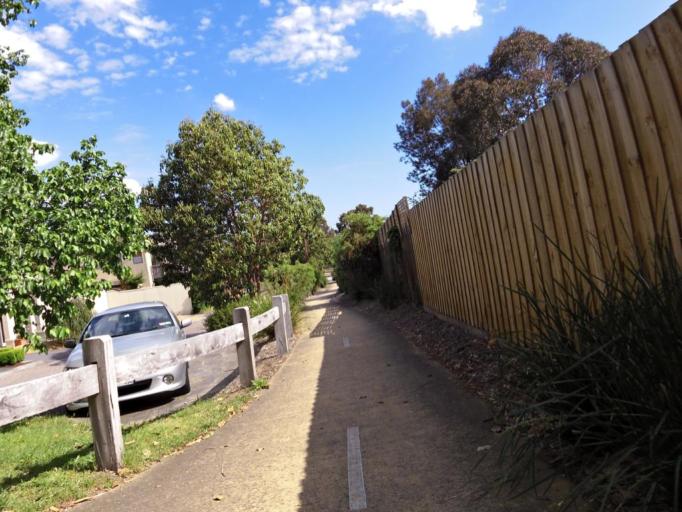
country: AU
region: Victoria
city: Rosanna
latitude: -37.7491
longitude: 145.0794
